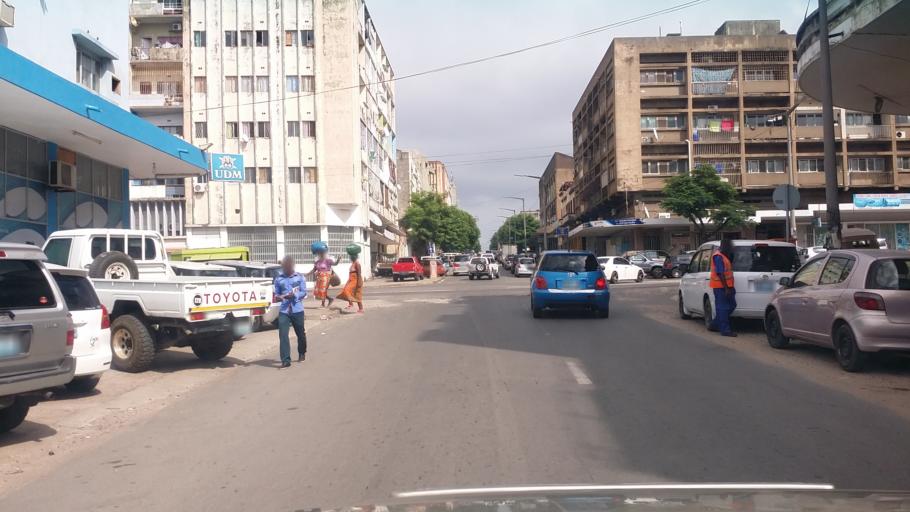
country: MZ
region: Maputo City
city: Maputo
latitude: -25.9658
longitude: 32.5675
